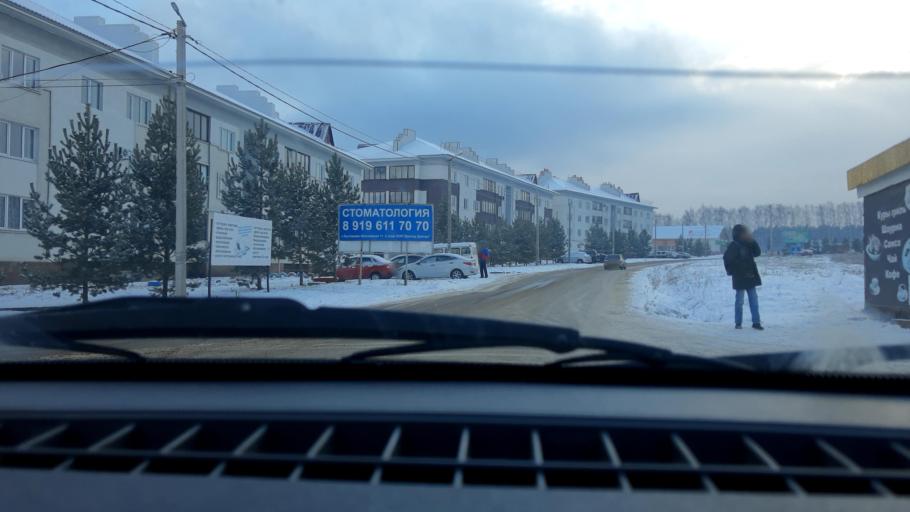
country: RU
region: Bashkortostan
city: Avdon
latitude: 54.4774
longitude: 55.8771
